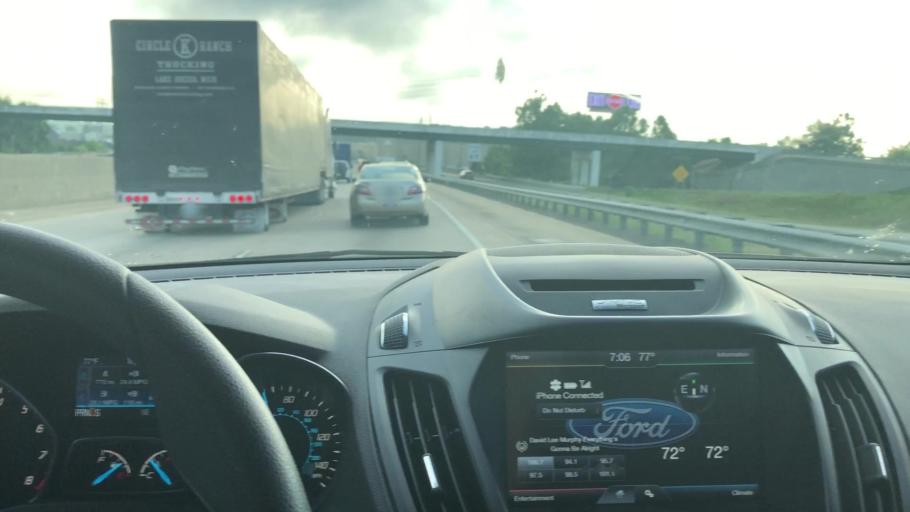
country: US
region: Arkansas
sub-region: Pulaski County
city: Alexander
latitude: 34.6484
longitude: -92.4189
